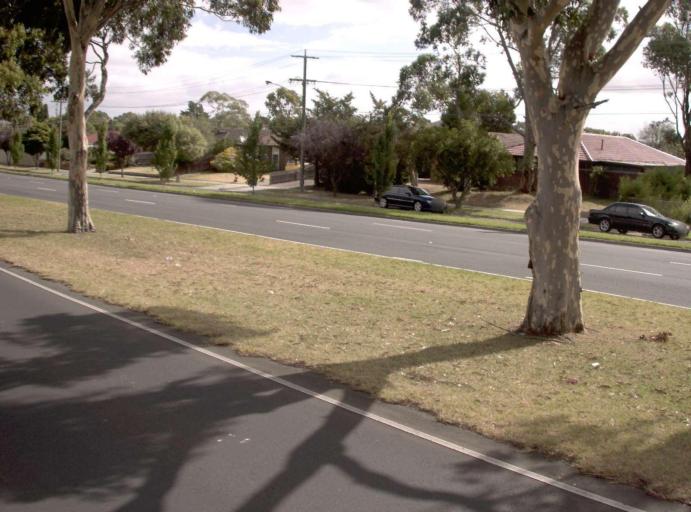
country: AU
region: Victoria
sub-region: Greater Dandenong
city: Dandenong North
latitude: -37.9680
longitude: 145.2240
